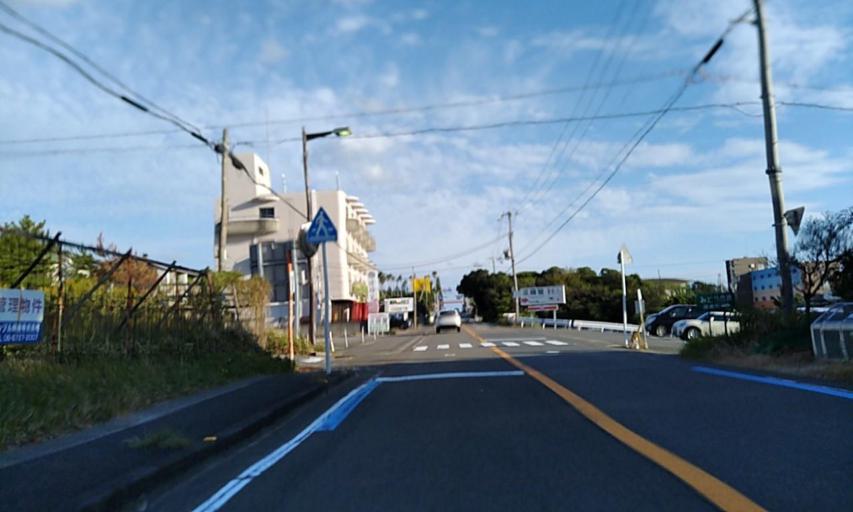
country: JP
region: Wakayama
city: Tanabe
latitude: 33.6676
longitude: 135.3351
